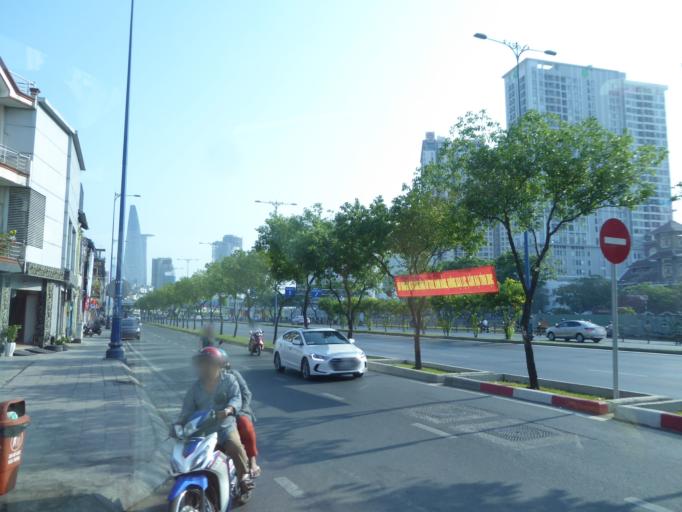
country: VN
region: Ho Chi Minh City
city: Quan Sau
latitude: 10.7079
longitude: 106.6759
